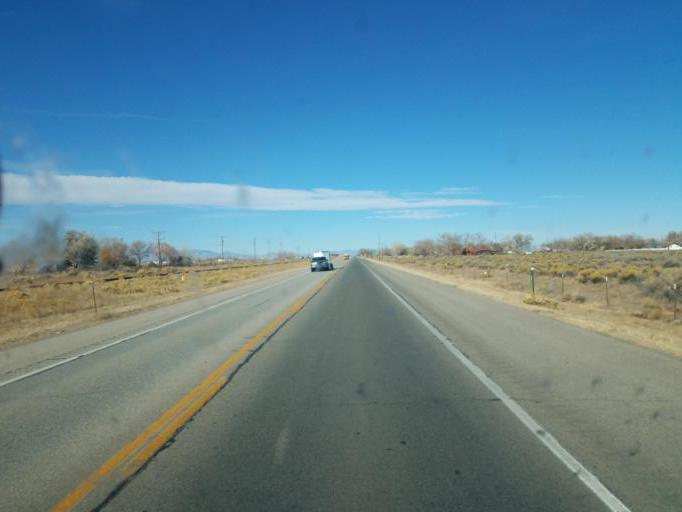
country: US
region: Colorado
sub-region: Alamosa County
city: Alamosa
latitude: 37.4934
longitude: -105.9375
